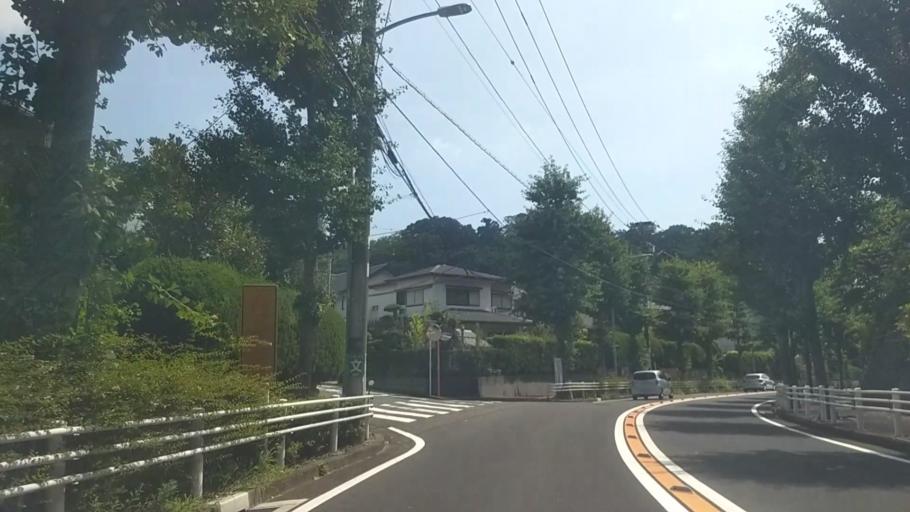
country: JP
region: Kanagawa
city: Yokosuka
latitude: 35.3466
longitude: 139.6315
